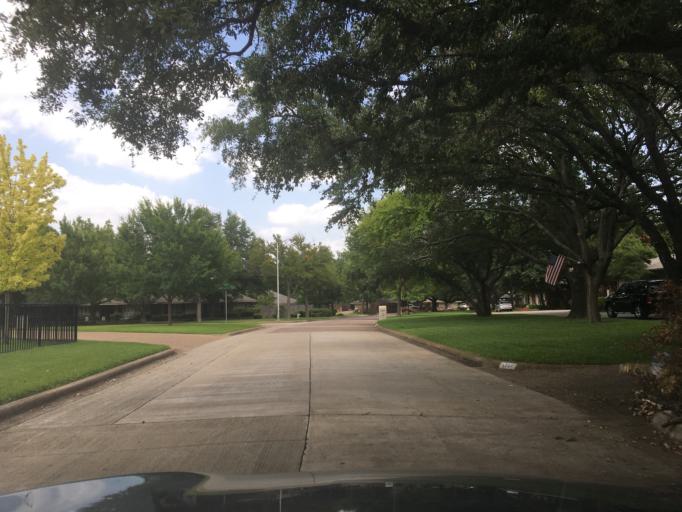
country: US
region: Texas
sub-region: Dallas County
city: University Park
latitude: 32.8991
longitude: -96.8139
